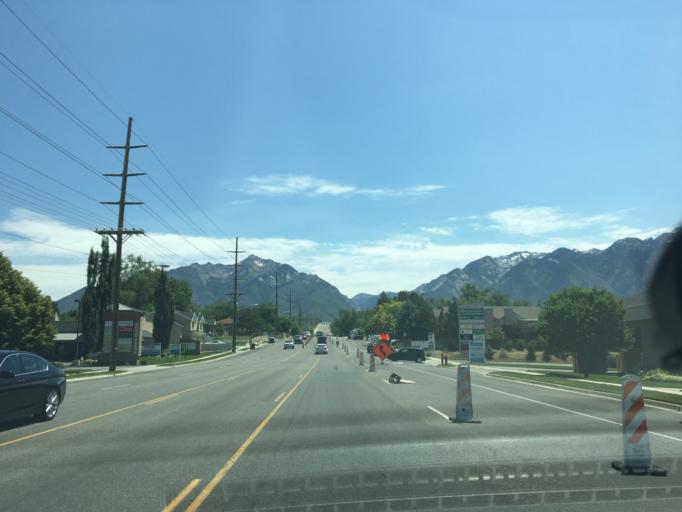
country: US
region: Utah
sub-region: Salt Lake County
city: White City
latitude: 40.5806
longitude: -111.8674
